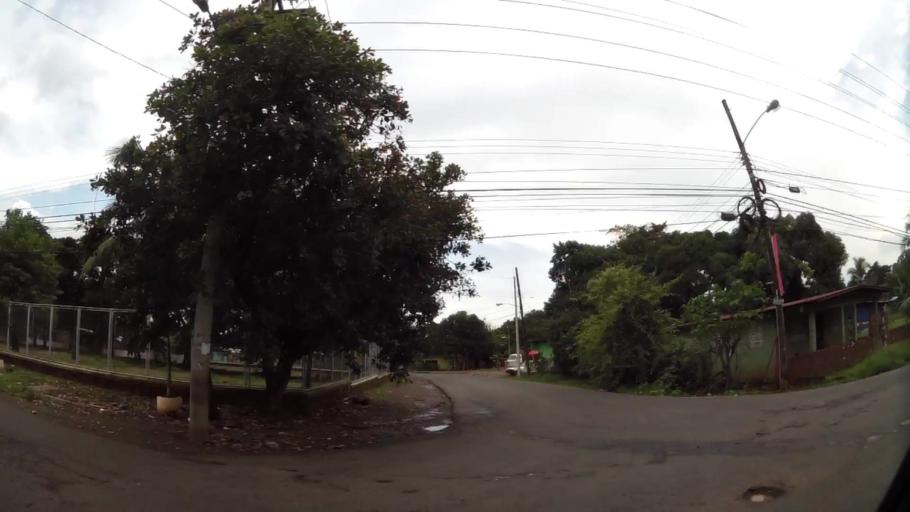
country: PA
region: Panama
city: Cabra Numero Uno
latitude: 9.1123
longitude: -79.3440
